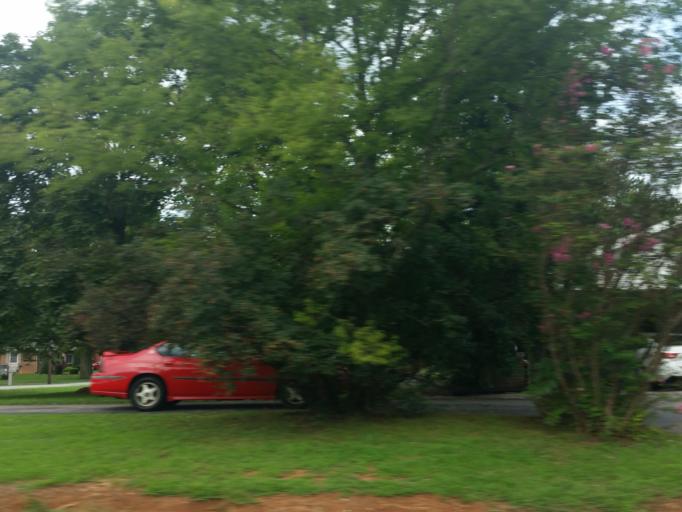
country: US
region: Kentucky
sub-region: Christian County
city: Hopkinsville
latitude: 36.8514
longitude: -87.5153
